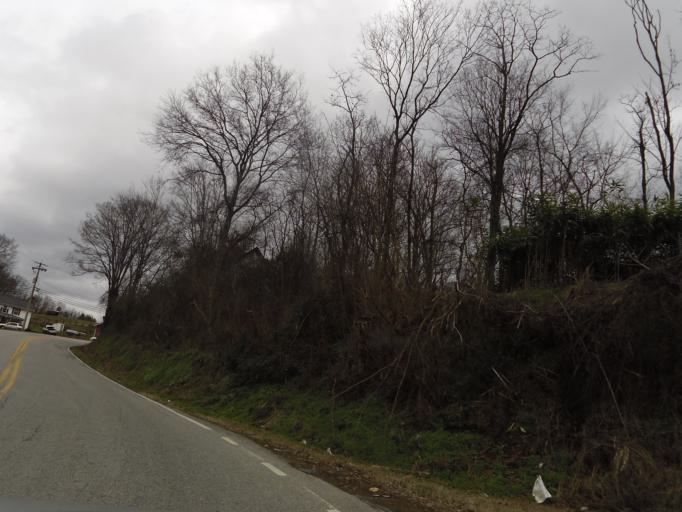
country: US
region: Tennessee
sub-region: Grainger County
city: Blaine
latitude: 36.1376
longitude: -83.6656
